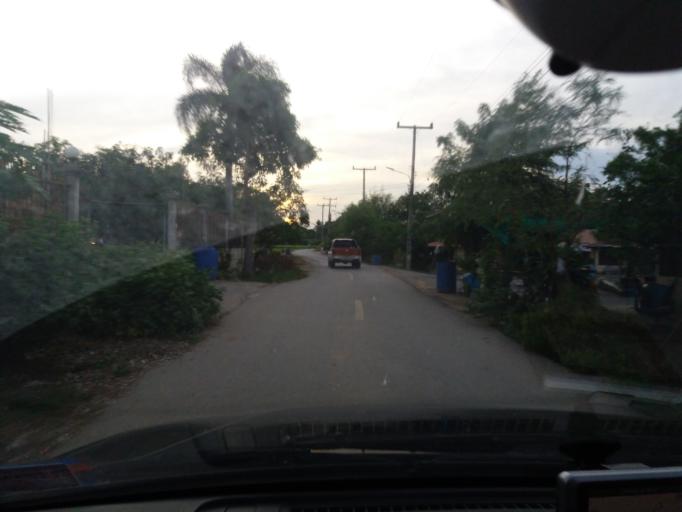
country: TH
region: Suphan Buri
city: Doembang Nangbuat
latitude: 14.8113
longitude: 100.1410
